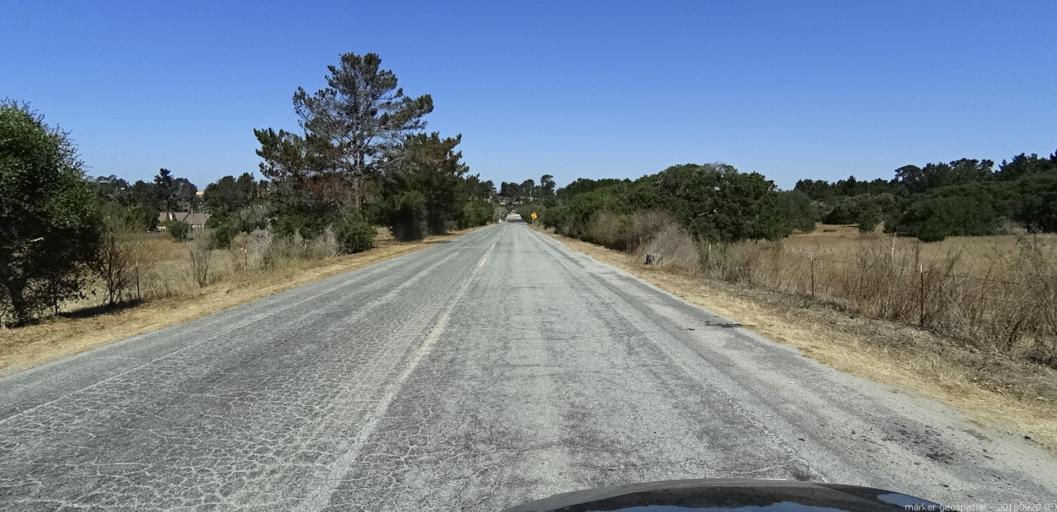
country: US
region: California
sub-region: Monterey County
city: Del Rey Oaks
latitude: 36.5812
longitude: -121.8498
